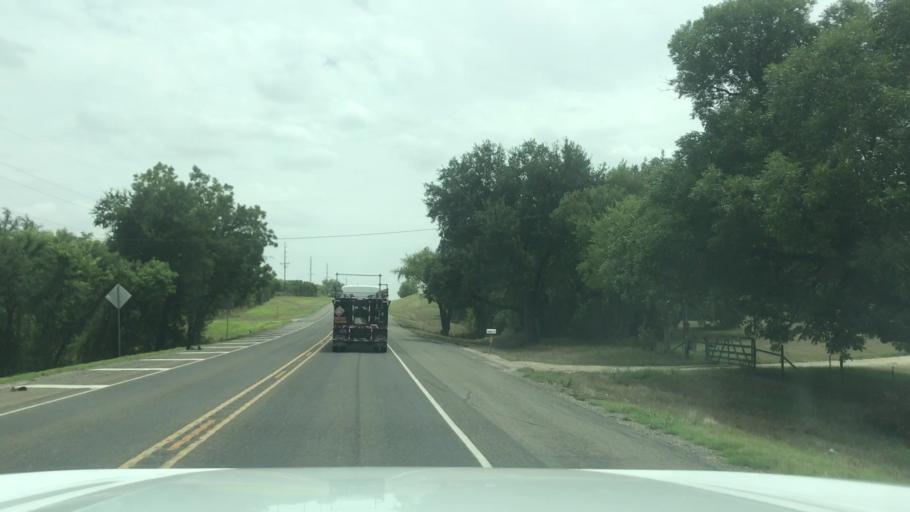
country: US
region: Texas
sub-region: Bosque County
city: Valley Mills
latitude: 31.6925
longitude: -97.5345
